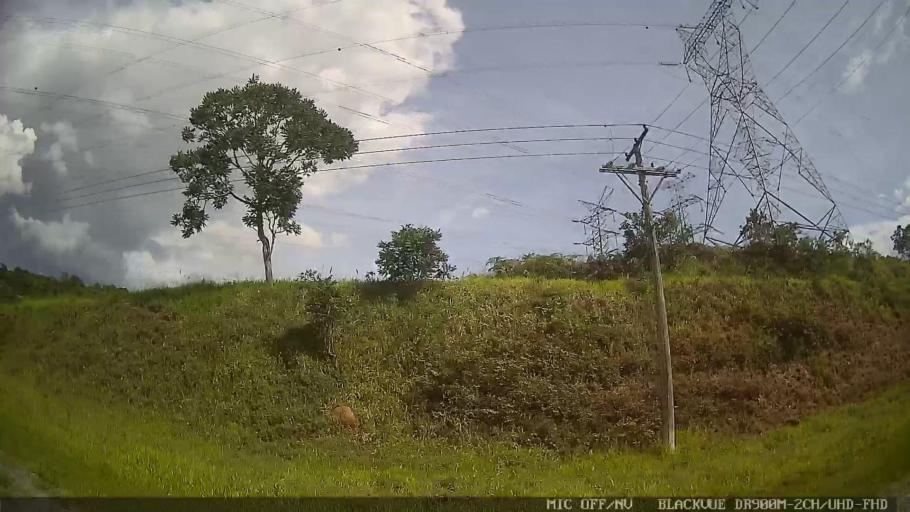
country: BR
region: Sao Paulo
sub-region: Mogi das Cruzes
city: Mogi das Cruzes
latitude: -23.6175
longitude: -46.1974
